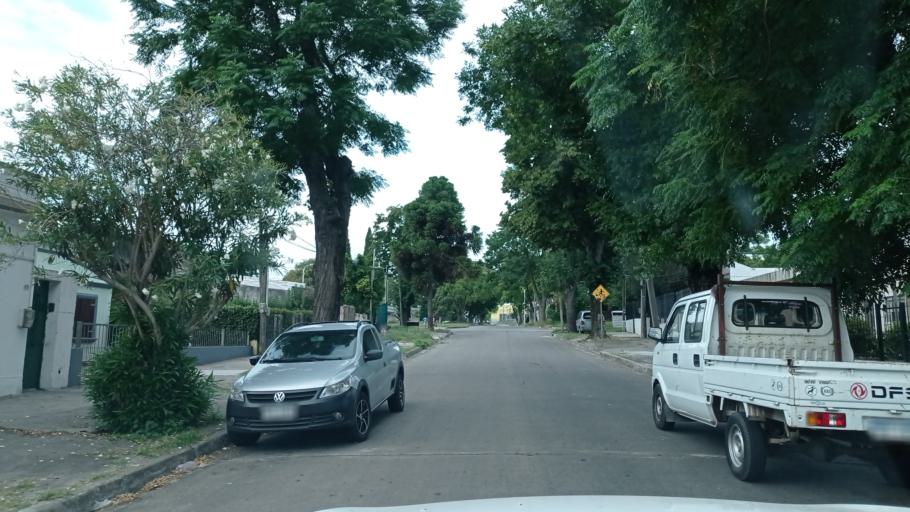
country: UY
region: Montevideo
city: Montevideo
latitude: -34.8390
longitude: -56.2129
